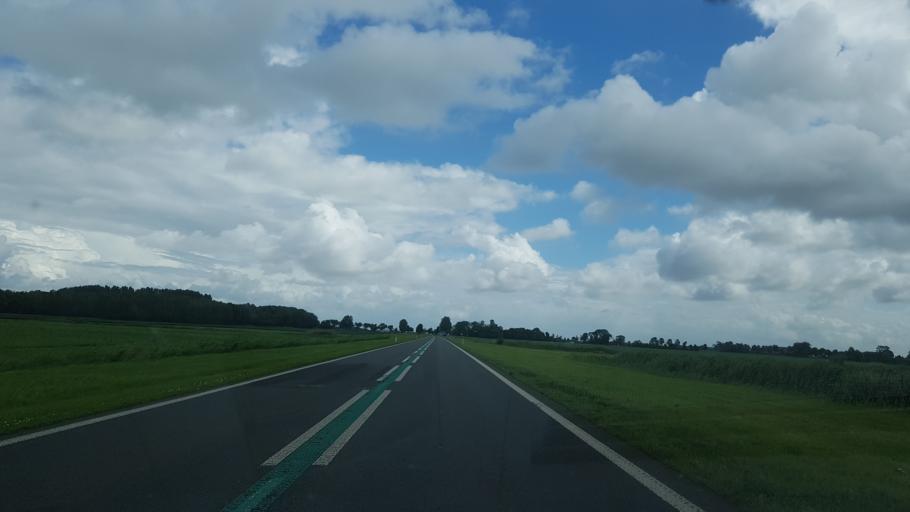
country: NL
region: Friesland
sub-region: Gemeente Dantumadiel
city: Walterswald
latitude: 53.3524
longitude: 6.0671
